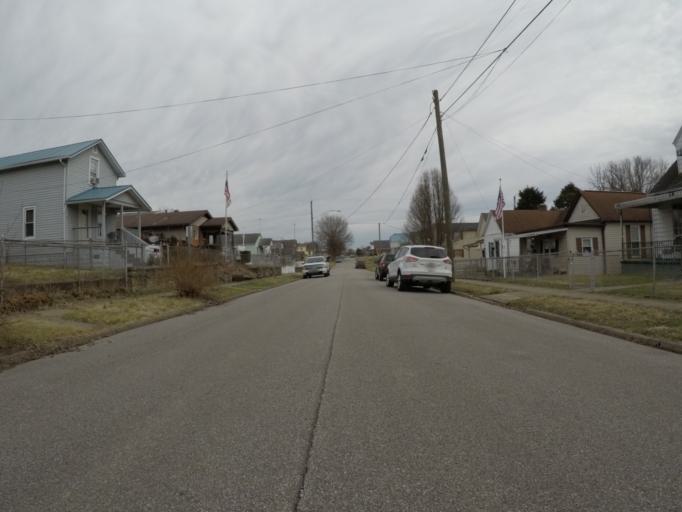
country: US
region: Ohio
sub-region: Lawrence County
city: Burlington
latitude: 38.4069
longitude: -82.4919
